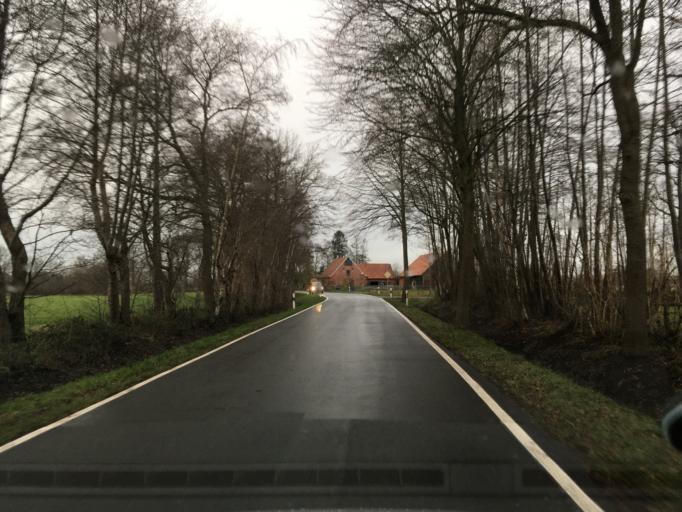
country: DE
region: North Rhine-Westphalia
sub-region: Regierungsbezirk Munster
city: Heek
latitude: 52.1584
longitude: 7.1402
